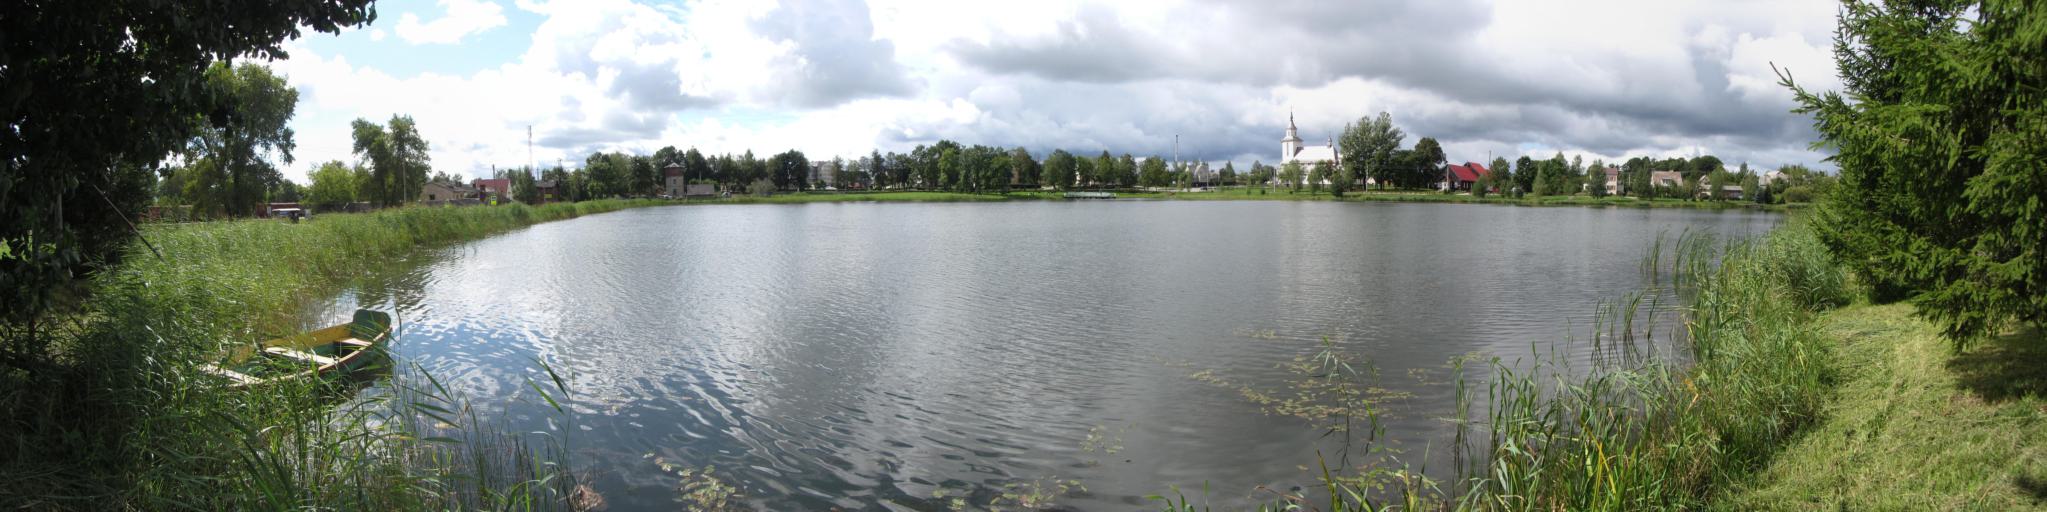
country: LT
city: Dukstas
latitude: 55.5220
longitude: 26.3254
